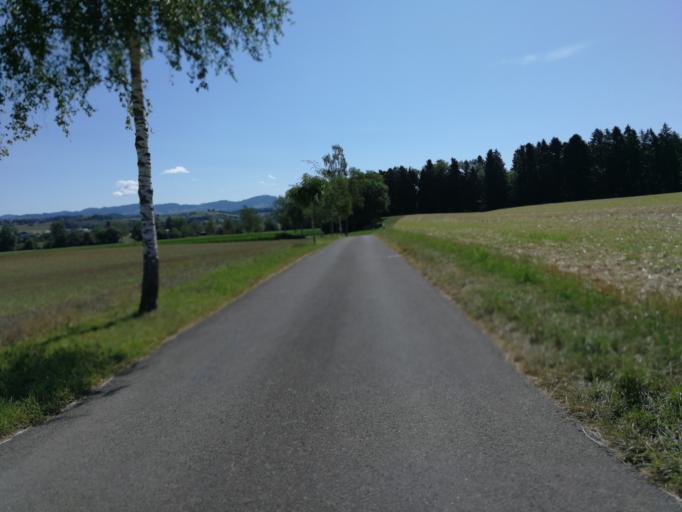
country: CH
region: Zurich
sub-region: Bezirk Hinwil
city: Gossau
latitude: 47.2934
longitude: 8.7459
